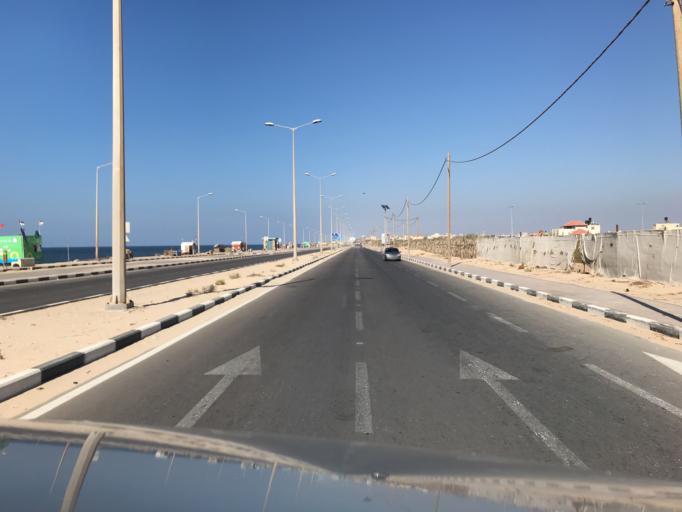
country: PS
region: Gaza Strip
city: An Nusayrat
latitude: 31.4707
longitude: 34.3830
